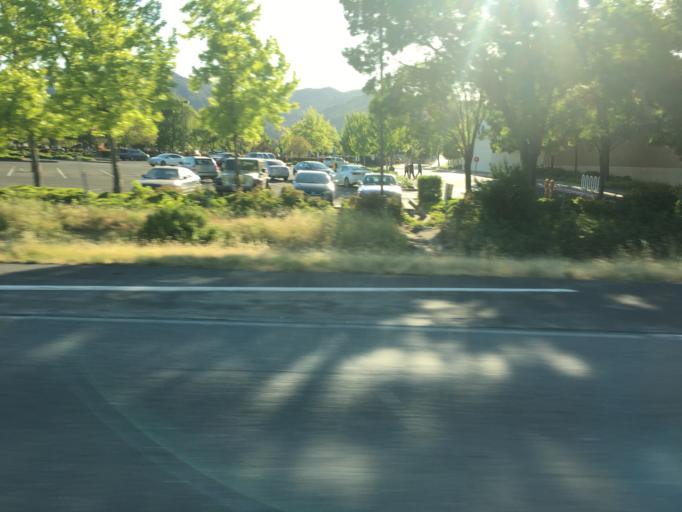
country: US
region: California
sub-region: Mendocino County
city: Ukiah
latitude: 39.1552
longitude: -123.1975
